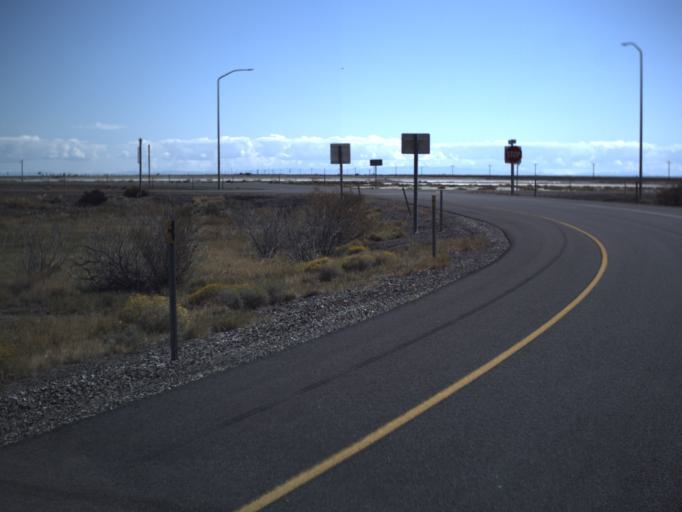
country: US
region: Utah
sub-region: Tooele County
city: Wendover
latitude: 40.7401
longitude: -113.9716
